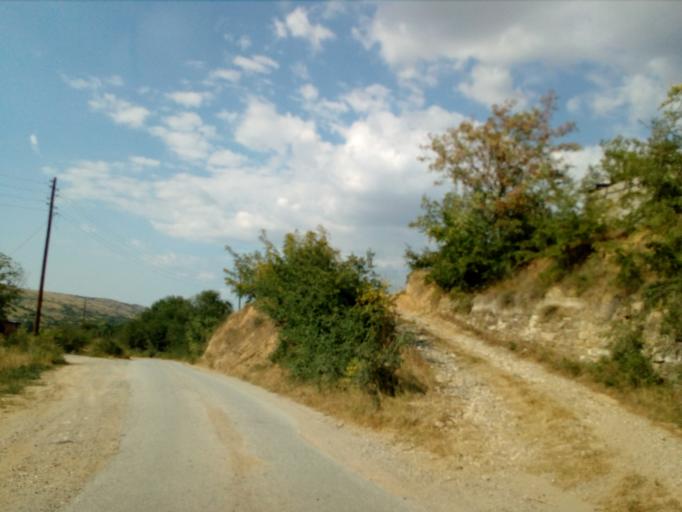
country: MK
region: Veles
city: Veles
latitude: 41.7340
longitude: 21.7887
